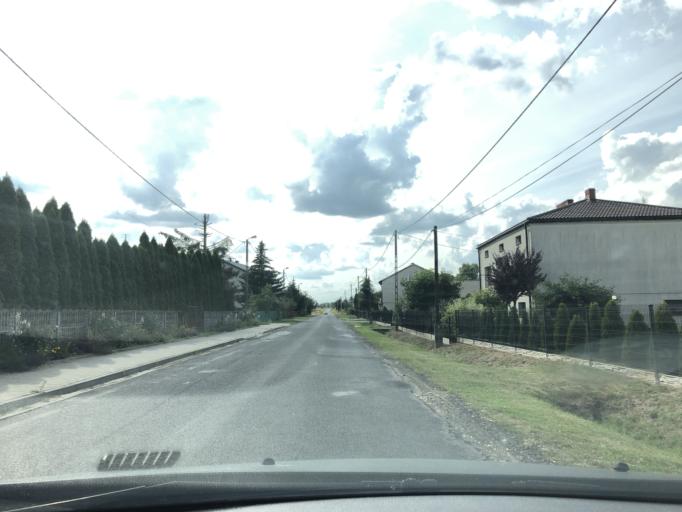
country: PL
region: Lodz Voivodeship
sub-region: Powiat wieruszowski
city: Walichnowy
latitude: 51.2614
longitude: 18.3864
